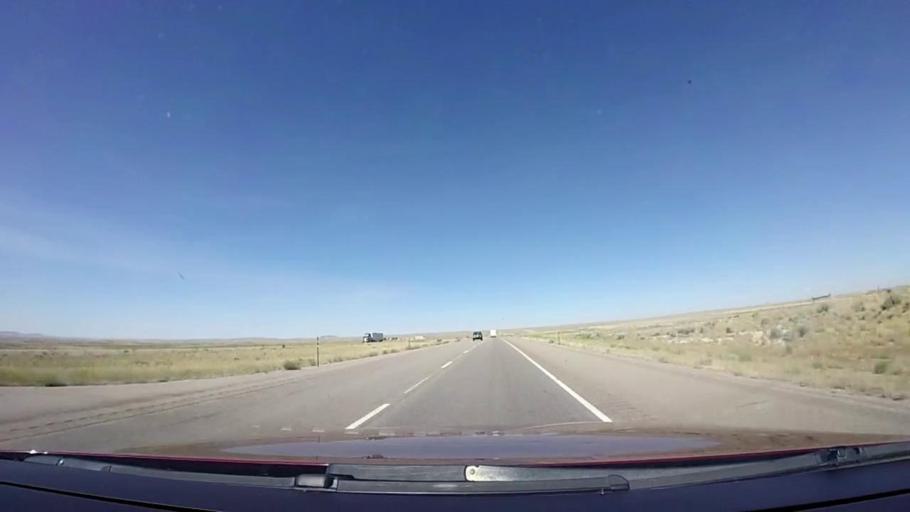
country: US
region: Wyoming
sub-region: Sweetwater County
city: Rock Springs
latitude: 41.6394
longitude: -108.4725
